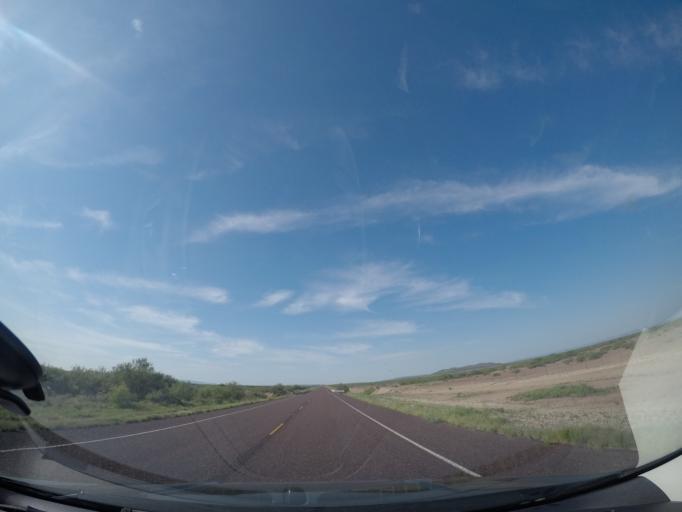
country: US
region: Texas
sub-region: Brewster County
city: Alpine
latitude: 29.8689
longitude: -103.5775
